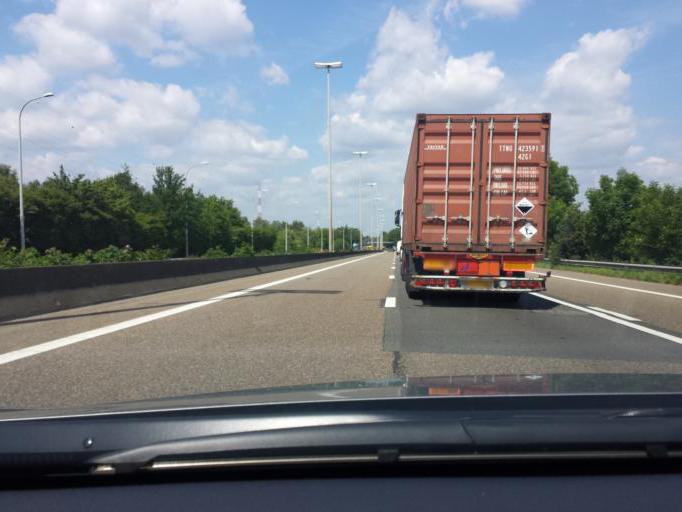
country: BE
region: Flanders
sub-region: Provincie Limburg
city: Hasselt
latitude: 50.9463
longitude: 5.2865
